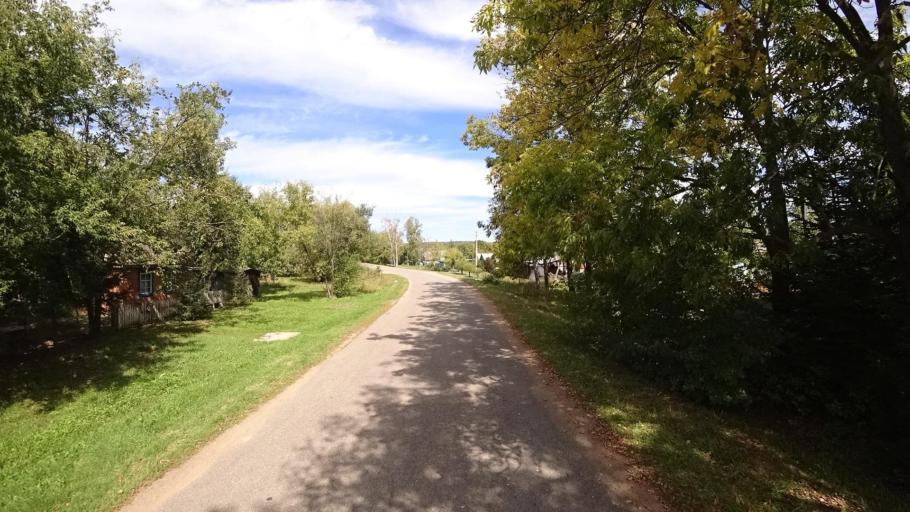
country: RU
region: Primorskiy
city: Yakovlevka
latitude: 44.6457
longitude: 133.5962
